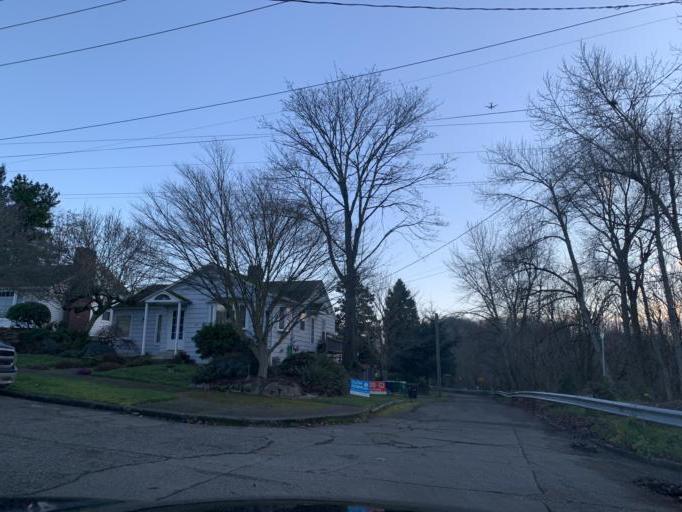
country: US
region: Washington
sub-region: King County
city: Seattle
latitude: 47.5753
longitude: -122.3161
